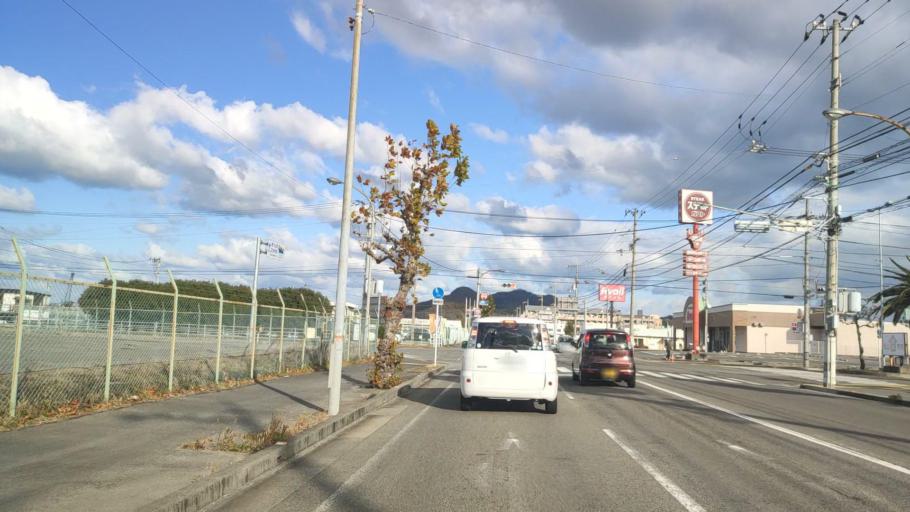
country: JP
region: Ehime
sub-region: Shikoku-chuo Shi
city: Matsuyama
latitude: 33.8568
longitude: 132.7127
